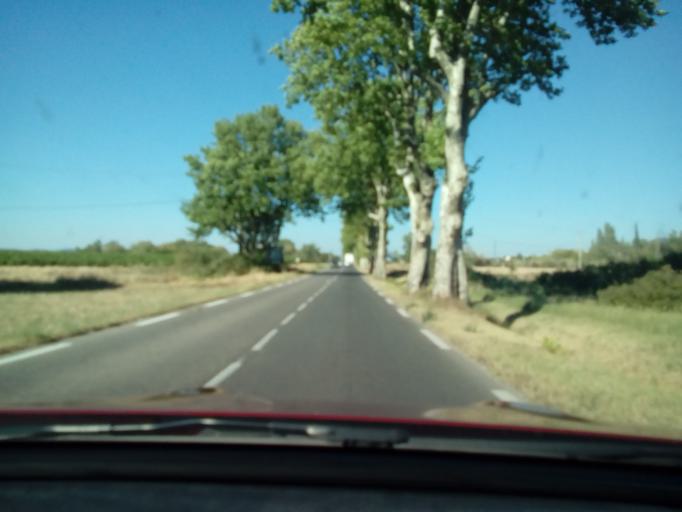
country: FR
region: Provence-Alpes-Cote d'Azur
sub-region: Departement des Bouches-du-Rhone
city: Trets
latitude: 43.4521
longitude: 5.6958
